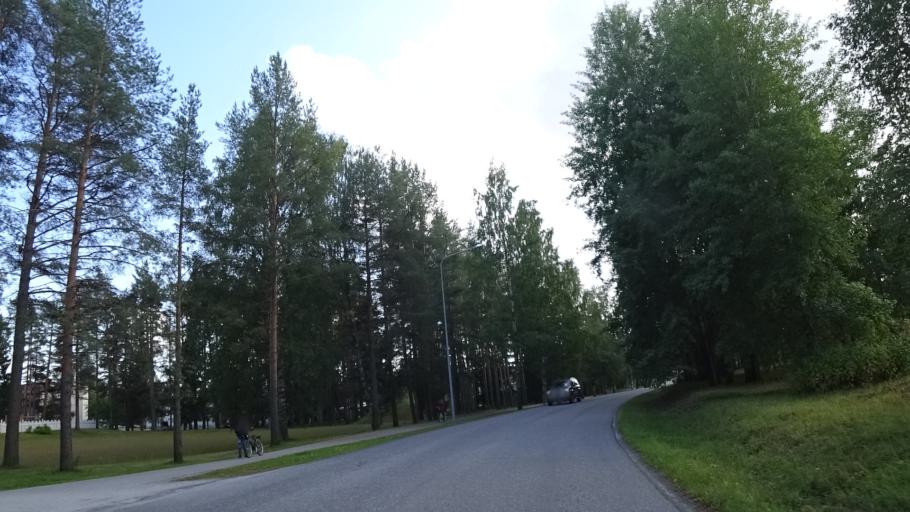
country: FI
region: North Karelia
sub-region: Pielisen Karjala
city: Lieksa
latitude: 63.3315
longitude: 30.0293
